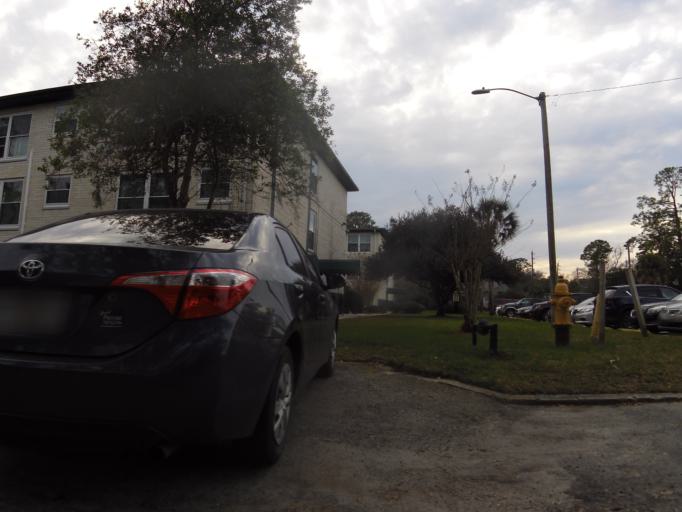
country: US
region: Florida
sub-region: Duval County
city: Jacksonville
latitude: 30.2491
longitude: -81.6310
